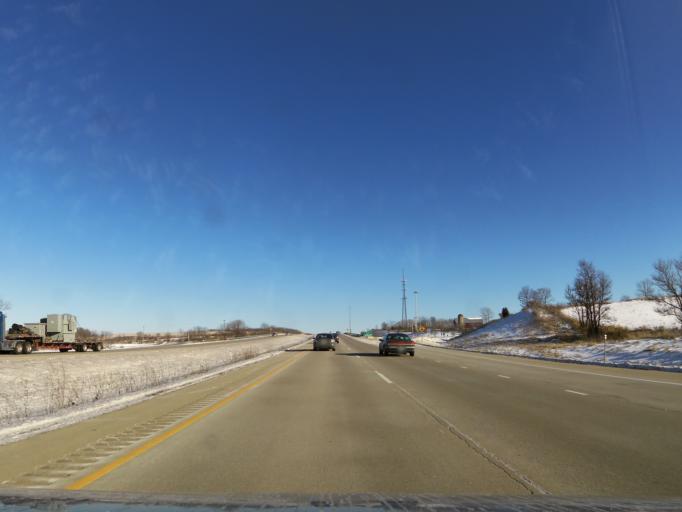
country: US
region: Wisconsin
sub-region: Dane County
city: Deerfield
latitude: 43.1092
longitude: -89.0867
